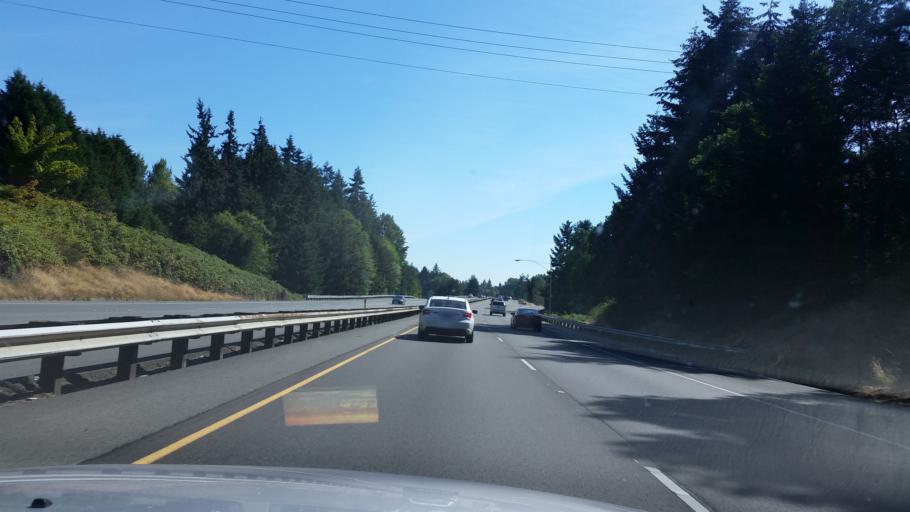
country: US
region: Washington
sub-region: King County
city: Boulevard Park
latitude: 47.4926
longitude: -122.3250
